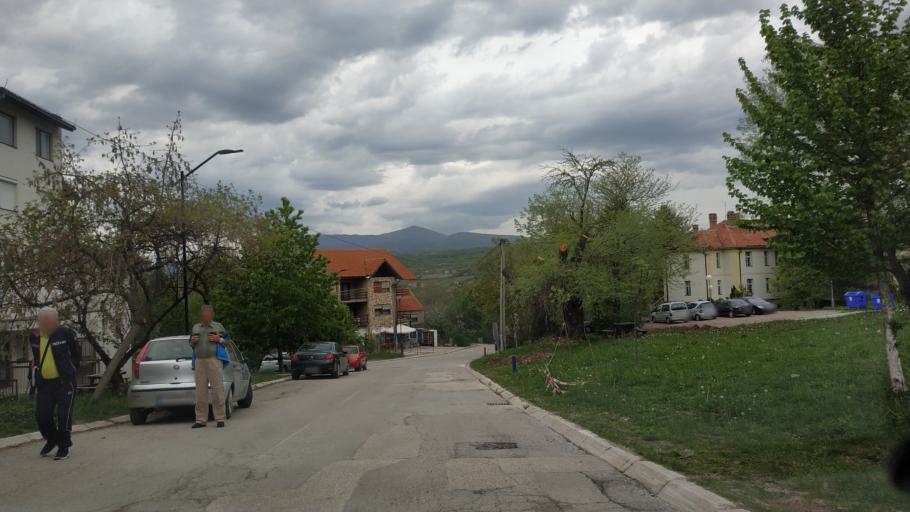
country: RS
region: Central Serbia
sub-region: Zajecarski Okrug
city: Soko Banja
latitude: 43.6405
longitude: 21.8705
